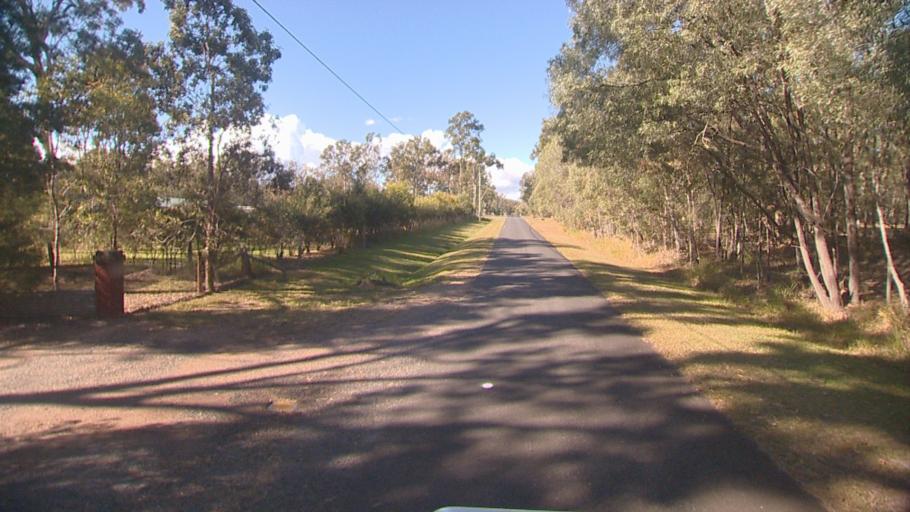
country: AU
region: Queensland
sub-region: Logan
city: Chambers Flat
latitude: -27.8011
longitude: 153.0655
